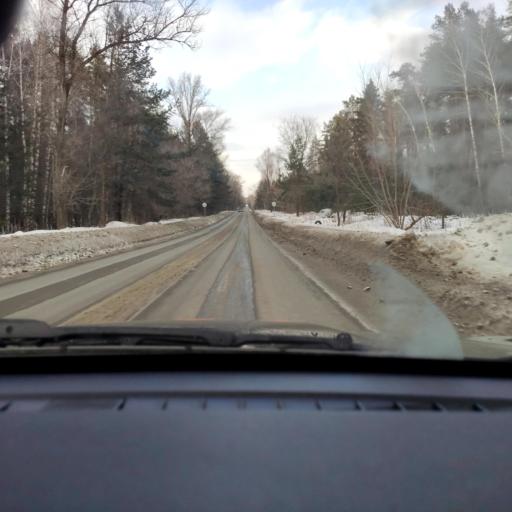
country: RU
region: Samara
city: Pribrezhnyy
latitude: 53.5026
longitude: 49.8492
